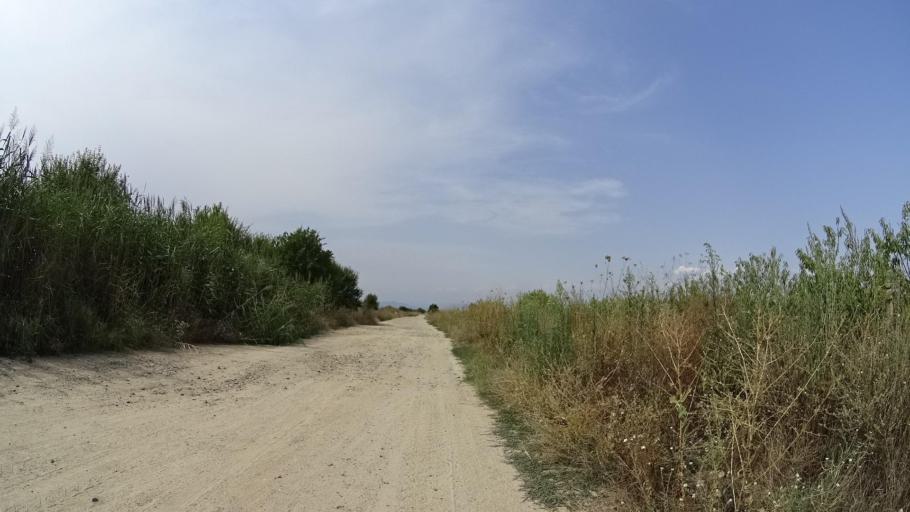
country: BG
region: Plovdiv
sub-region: Obshtina Kaloyanovo
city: Kaloyanovo
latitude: 42.2798
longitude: 24.7992
